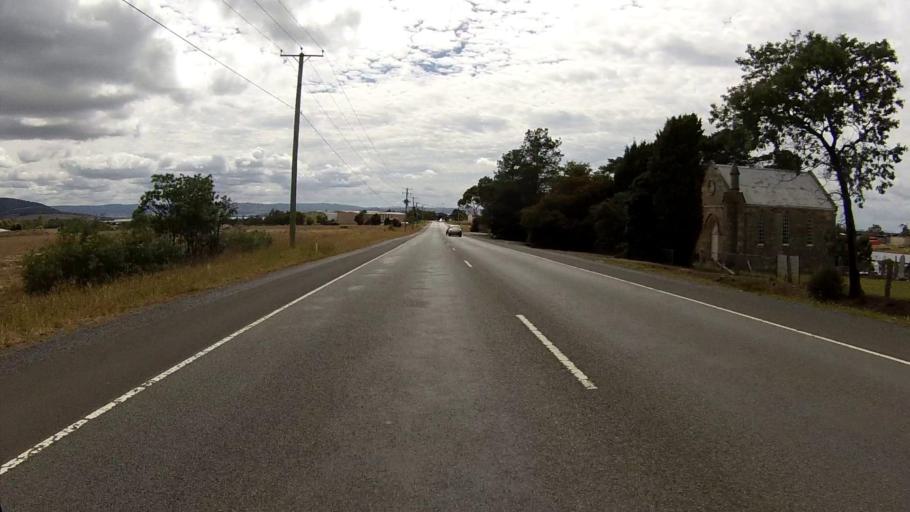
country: AU
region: Tasmania
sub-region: Clarence
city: Cambridge
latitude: -42.8326
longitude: 147.4596
